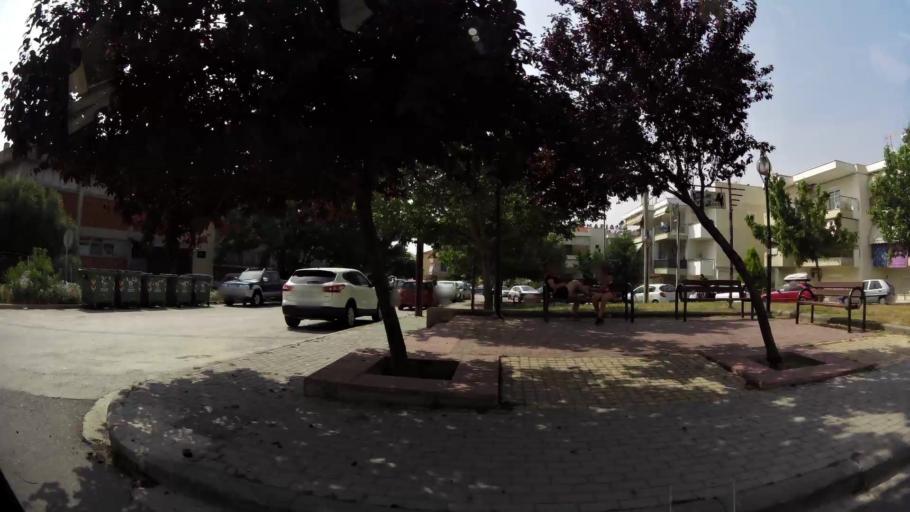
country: GR
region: Central Macedonia
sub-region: Nomos Thessalonikis
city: Efkarpia
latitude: 40.6830
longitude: 22.9461
